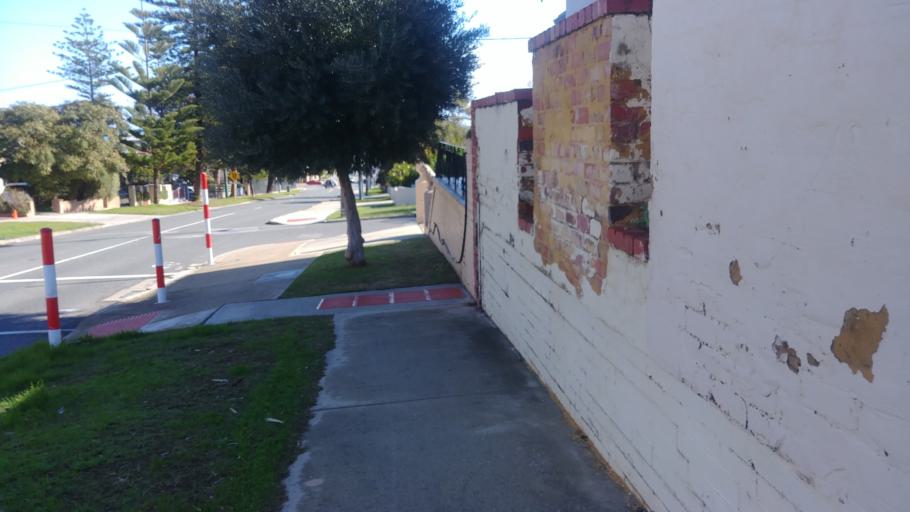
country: AU
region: Western Australia
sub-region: Fremantle
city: South Fremantle
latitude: -32.0675
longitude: 115.7598
